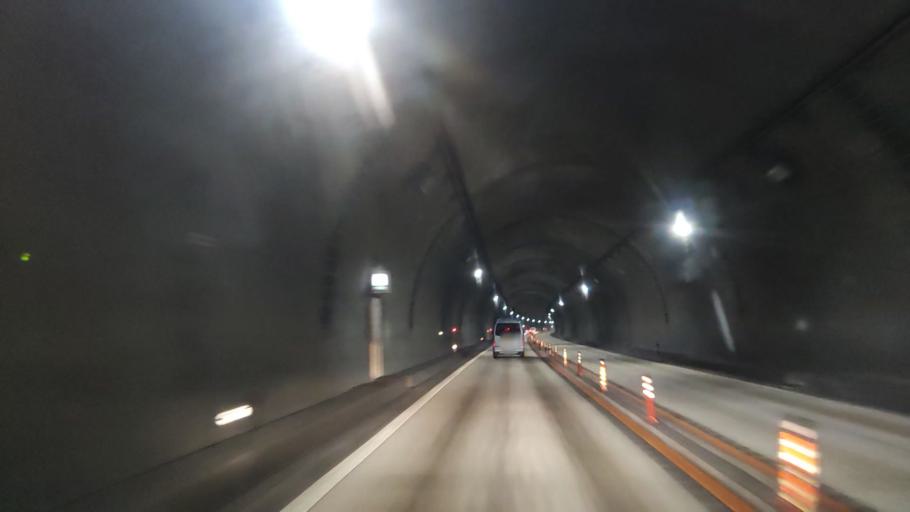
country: JP
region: Tokushima
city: Kamojimacho-jogejima
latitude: 34.1055
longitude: 134.3096
